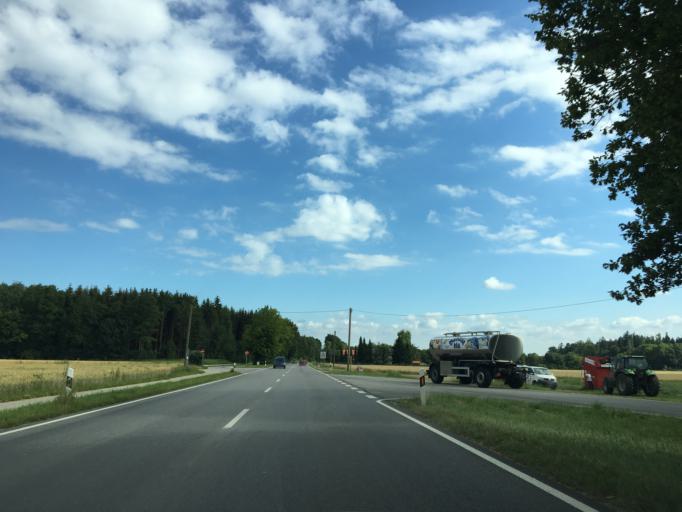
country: DE
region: Bavaria
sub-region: Upper Bavaria
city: Sauerlach
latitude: 47.9570
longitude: 11.6523
